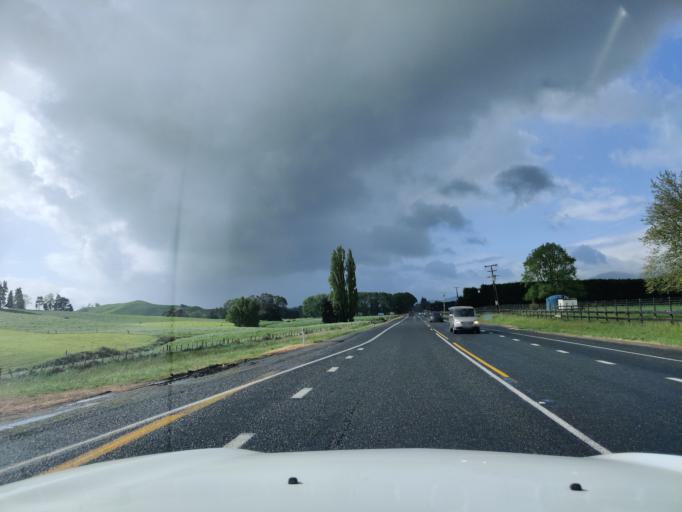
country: NZ
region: Waikato
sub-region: Waipa District
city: Cambridge
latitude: -37.9294
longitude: 175.5710
